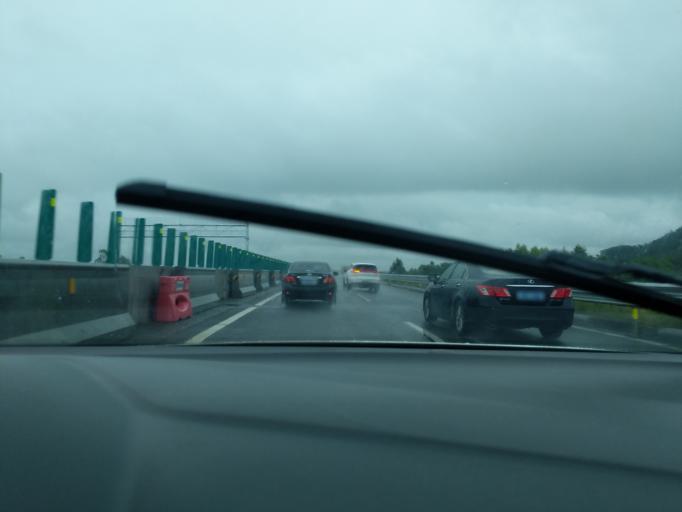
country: CN
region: Guangdong
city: Yueshan
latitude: 22.4645
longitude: 112.6990
